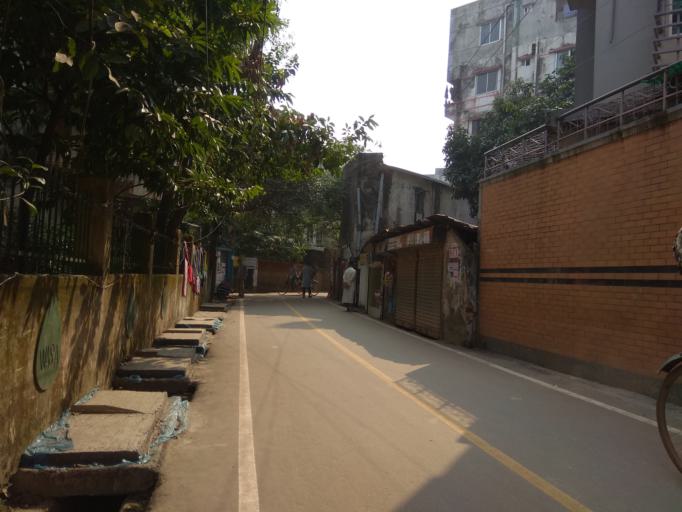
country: BD
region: Dhaka
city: Tungi
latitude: 23.8624
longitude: 90.3904
